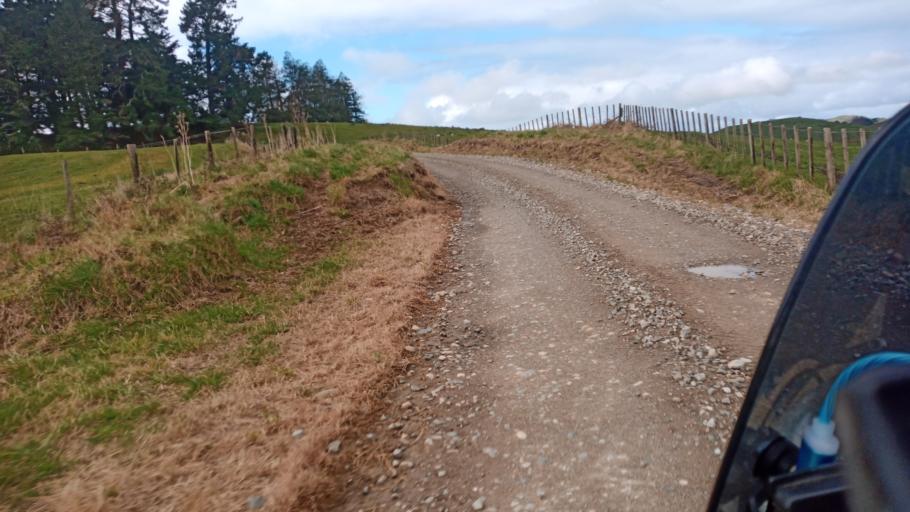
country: NZ
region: Gisborne
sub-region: Gisborne District
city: Gisborne
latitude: -38.5006
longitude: 178.2040
